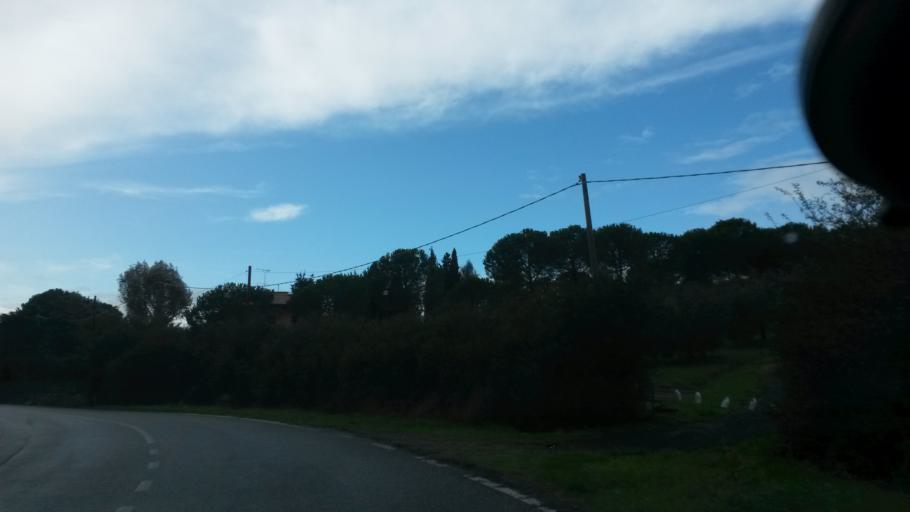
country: IT
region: Tuscany
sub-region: Provincia di Livorno
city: Rosignano Marittimo
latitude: 43.4188
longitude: 10.4561
